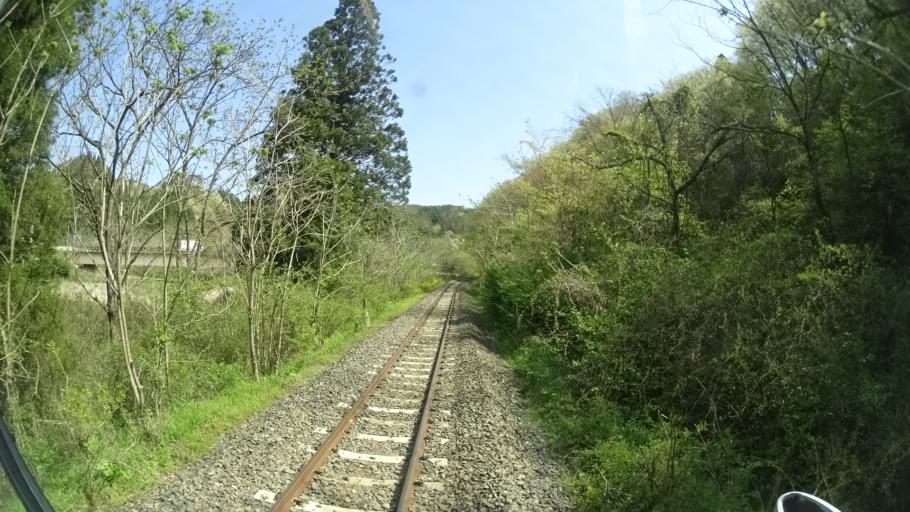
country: JP
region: Iwate
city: Ofunato
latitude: 38.9116
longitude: 141.5326
